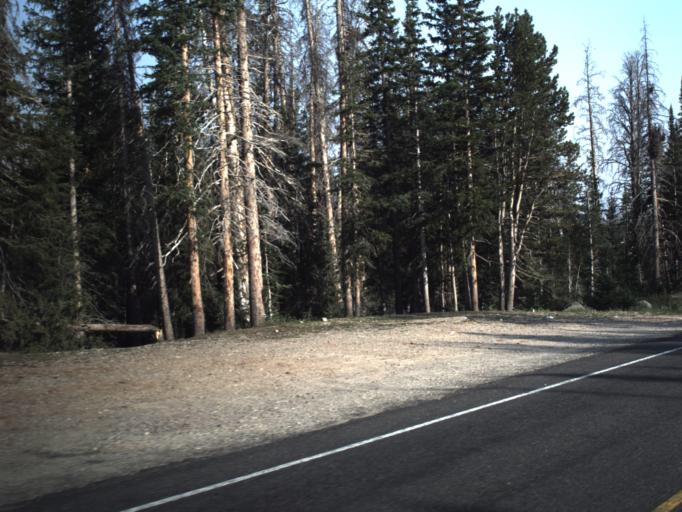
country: US
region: Utah
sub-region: Summit County
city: Kamas
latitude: 40.7167
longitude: -110.8770
